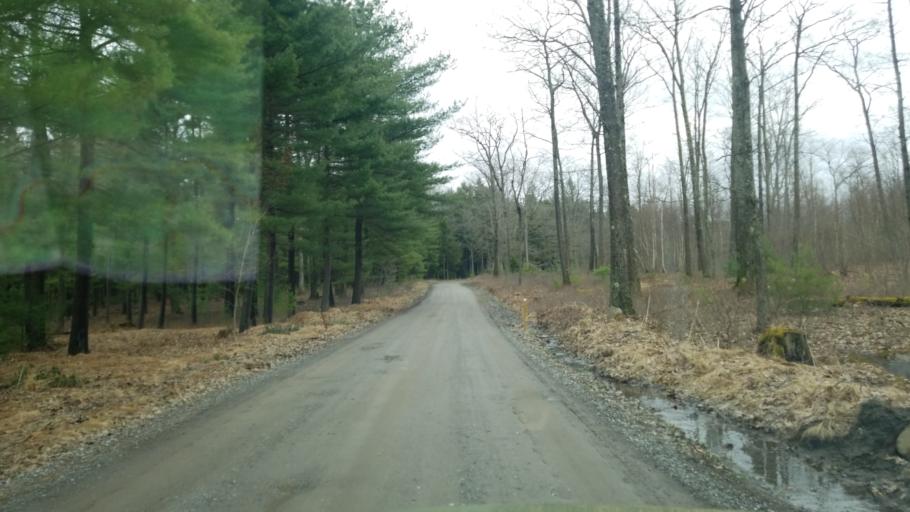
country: US
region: Pennsylvania
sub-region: Clearfield County
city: Shiloh
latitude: 41.1704
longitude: -78.2639
